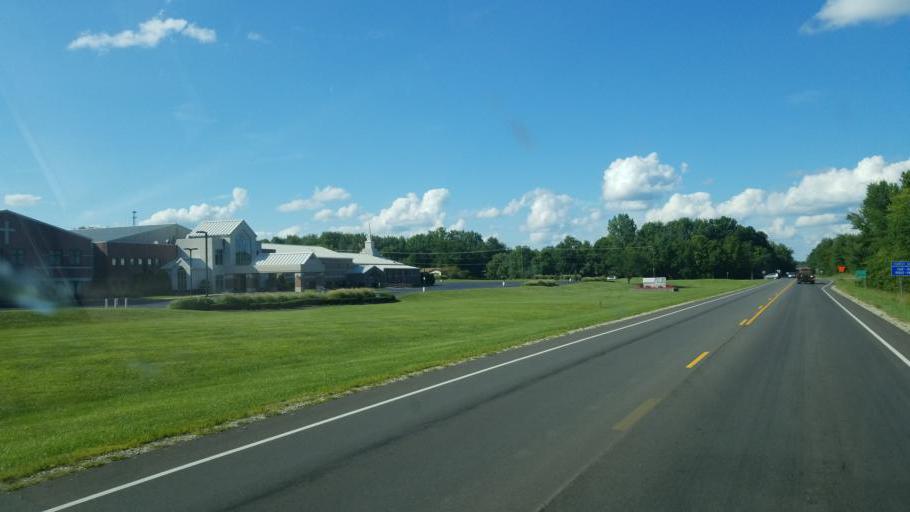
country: US
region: Ohio
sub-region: Delaware County
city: Sunbury
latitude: 40.1946
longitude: -82.9084
